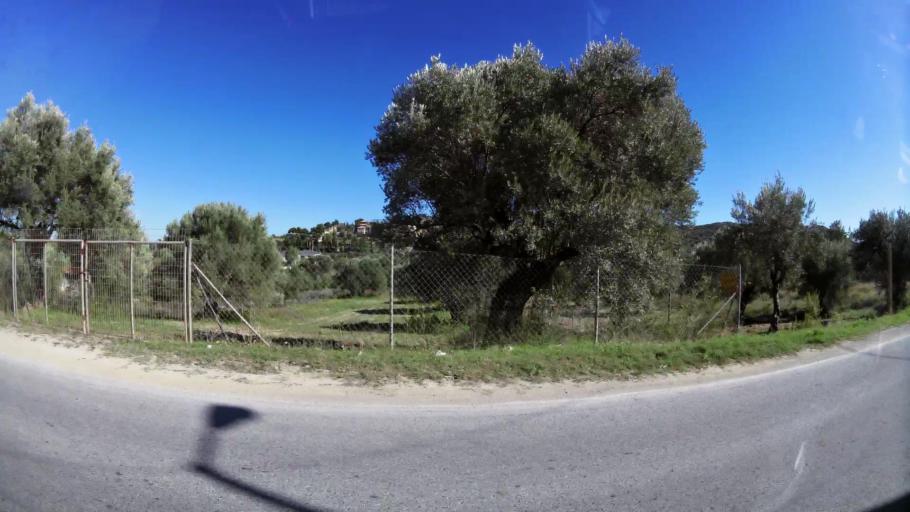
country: GR
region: Attica
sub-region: Nomarchia Anatolikis Attikis
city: Leondarion
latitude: 37.9714
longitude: 23.8626
